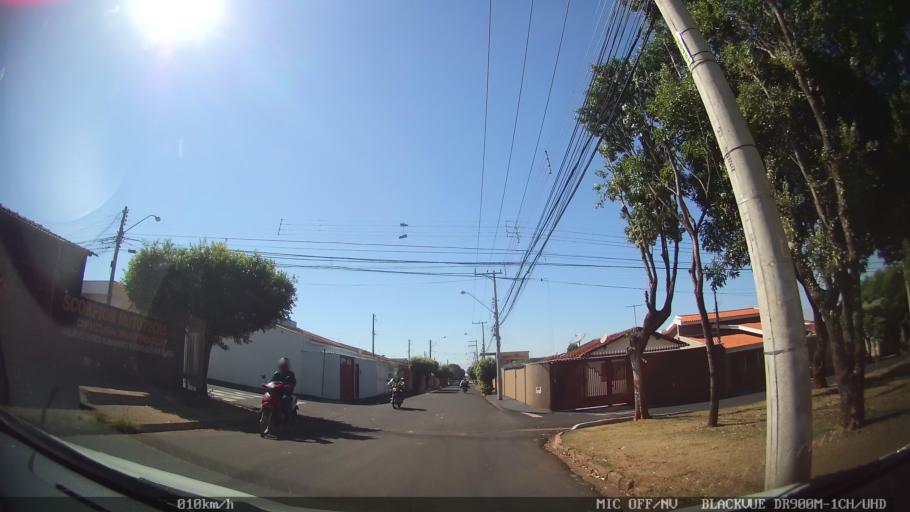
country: BR
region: Sao Paulo
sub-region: Sao Jose Do Rio Preto
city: Sao Jose do Rio Preto
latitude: -20.7702
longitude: -49.4096
